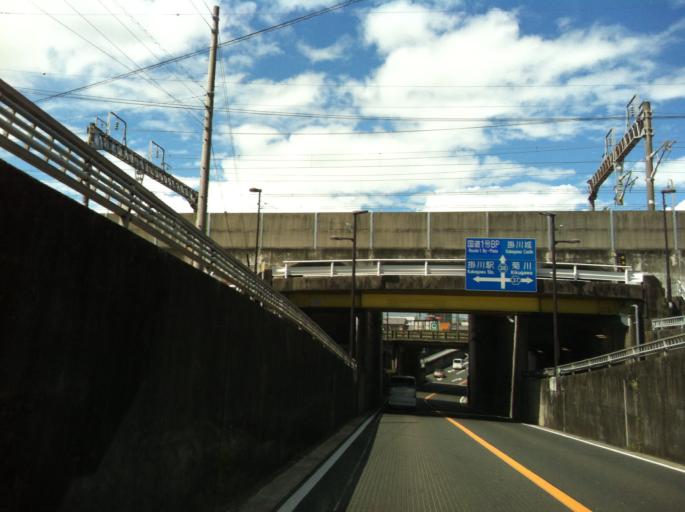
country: JP
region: Shizuoka
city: Kakegawa
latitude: 34.7694
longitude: 138.0189
